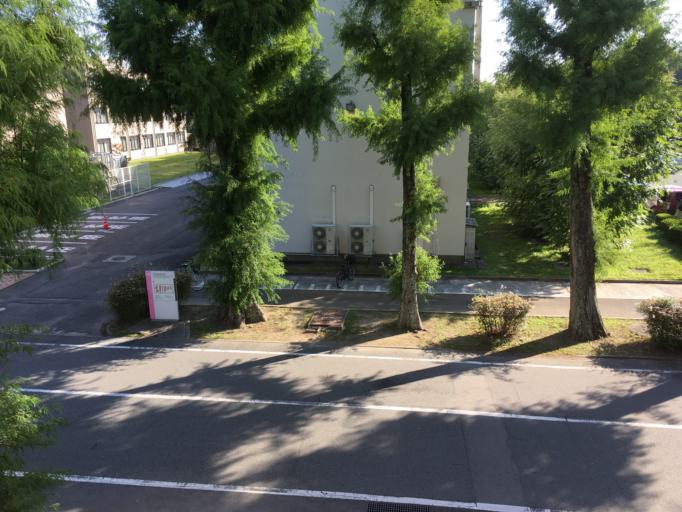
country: JP
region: Saga Prefecture
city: Saga-shi
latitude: 33.2424
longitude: 130.2928
